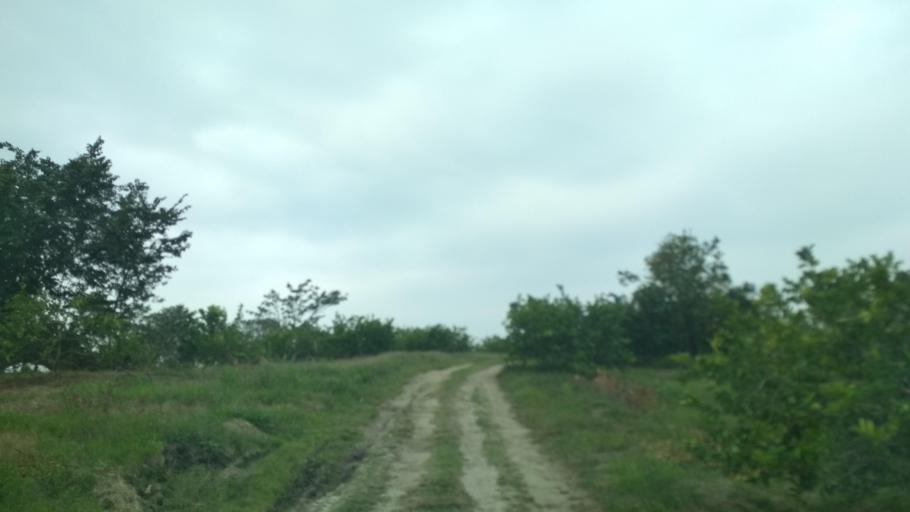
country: MM
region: Kayah
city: Loikaw
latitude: 20.2141
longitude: 97.3301
